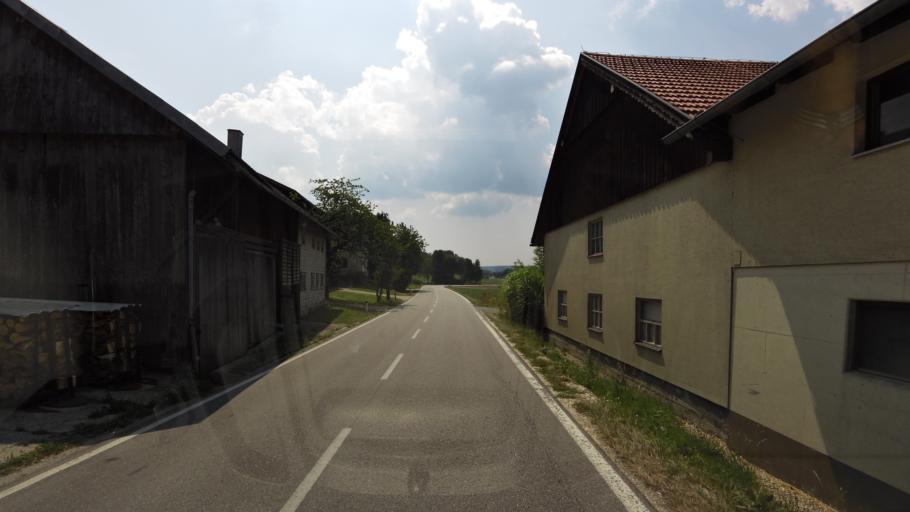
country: AT
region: Upper Austria
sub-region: Politischer Bezirk Ried im Innkreis
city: Waldzell
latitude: 48.1611
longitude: 13.4236
